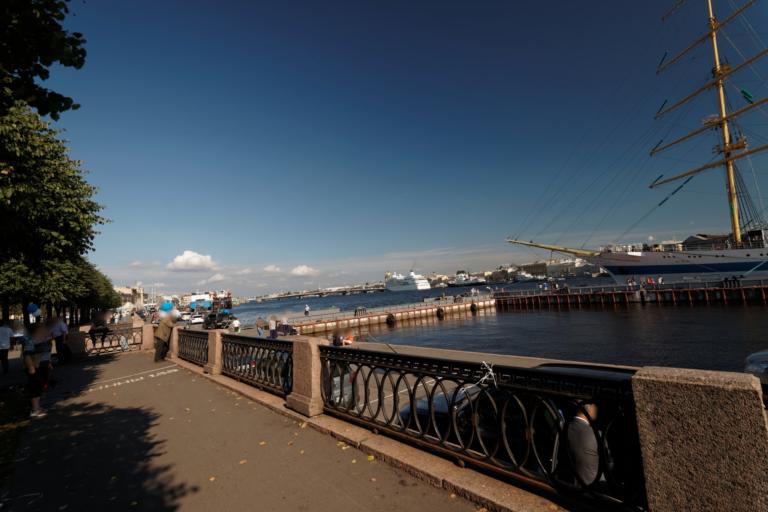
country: RU
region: St.-Petersburg
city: Vasyl'evsky Ostrov
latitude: 59.9331
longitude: 30.2762
